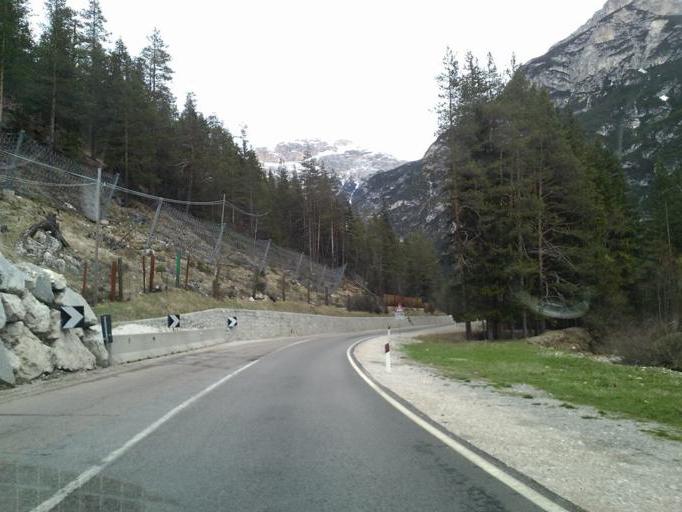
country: IT
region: Trentino-Alto Adige
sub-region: Bolzano
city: Dobbiaco
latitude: 46.6224
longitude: 12.2226
